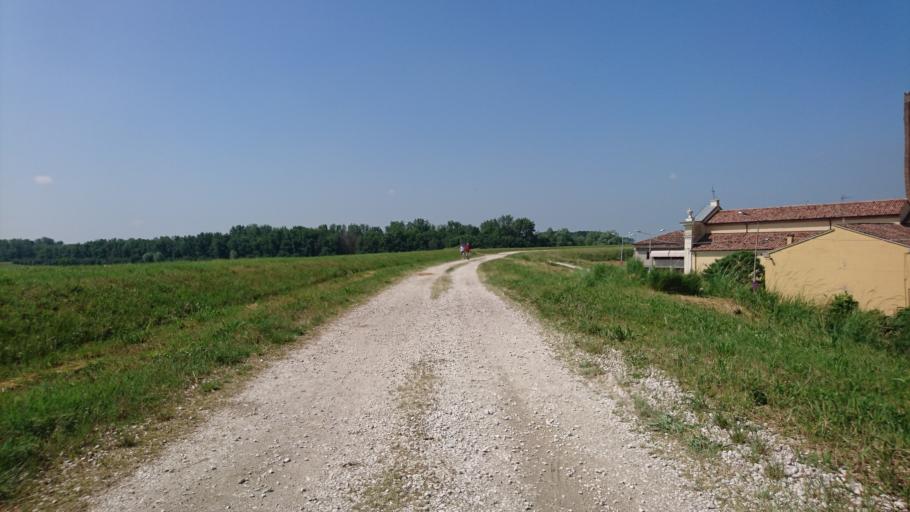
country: IT
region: Lombardy
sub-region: Provincia di Mantova
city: Quingentole
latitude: 45.0574
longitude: 11.0591
